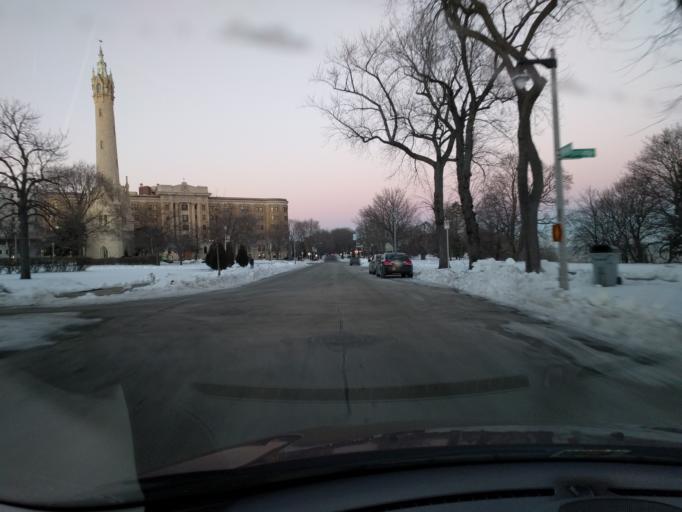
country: US
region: Wisconsin
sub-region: Milwaukee County
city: Shorewood
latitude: 43.0585
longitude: -87.8803
